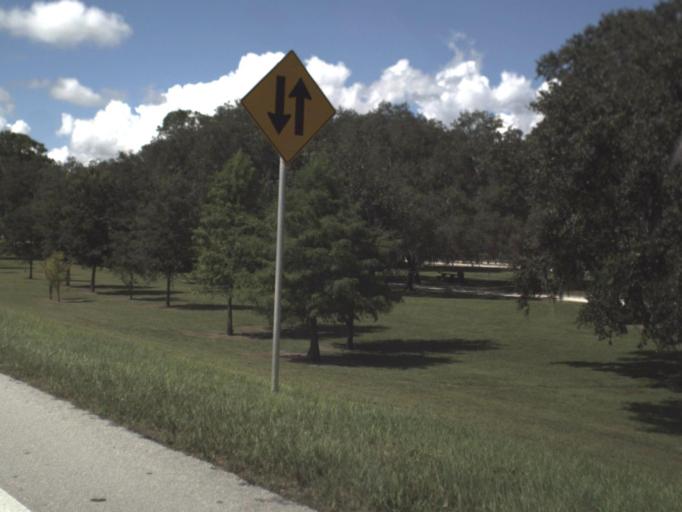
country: US
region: Florida
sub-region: DeSoto County
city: Arcadia
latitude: 27.2221
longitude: -81.8794
